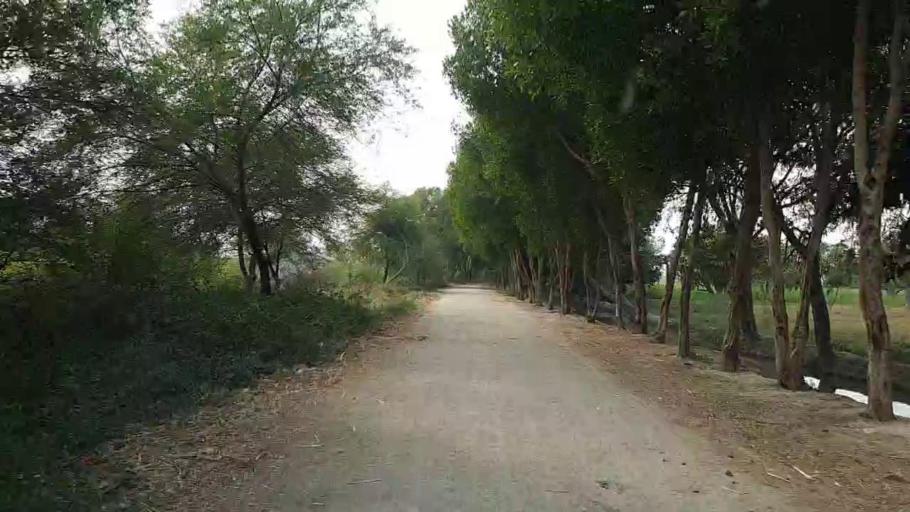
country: PK
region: Sindh
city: Mirwah Gorchani
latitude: 25.3804
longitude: 69.0628
